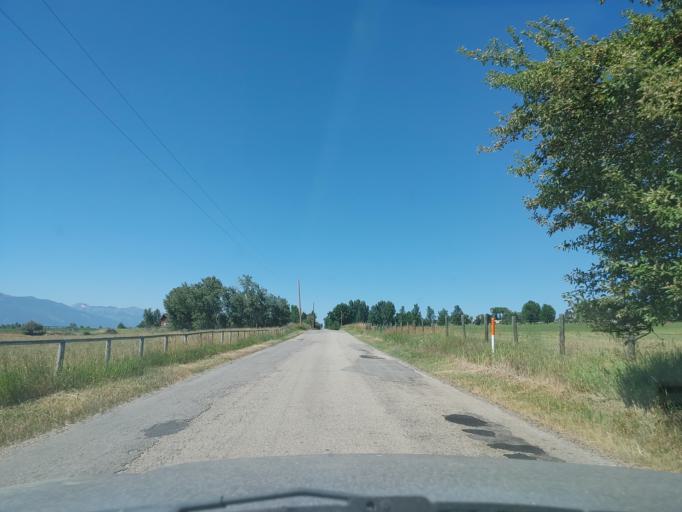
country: US
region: Montana
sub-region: Ravalli County
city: Hamilton
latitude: 46.3182
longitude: -114.0613
